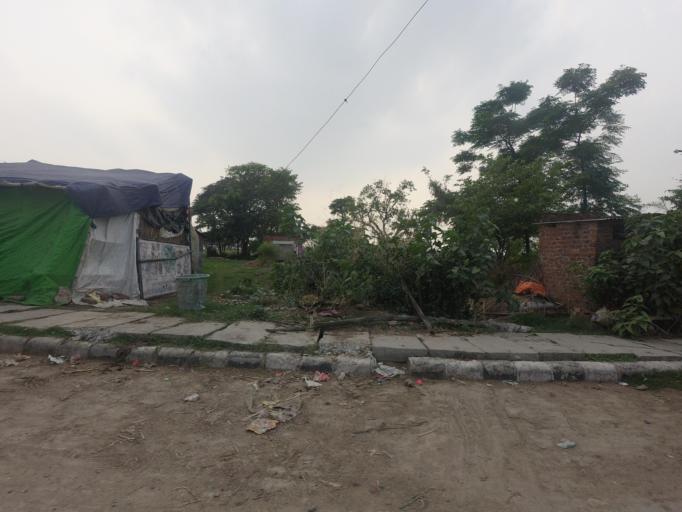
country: NP
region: Western Region
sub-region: Lumbini Zone
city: Bhairahawa
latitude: 27.5114
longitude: 83.4249
